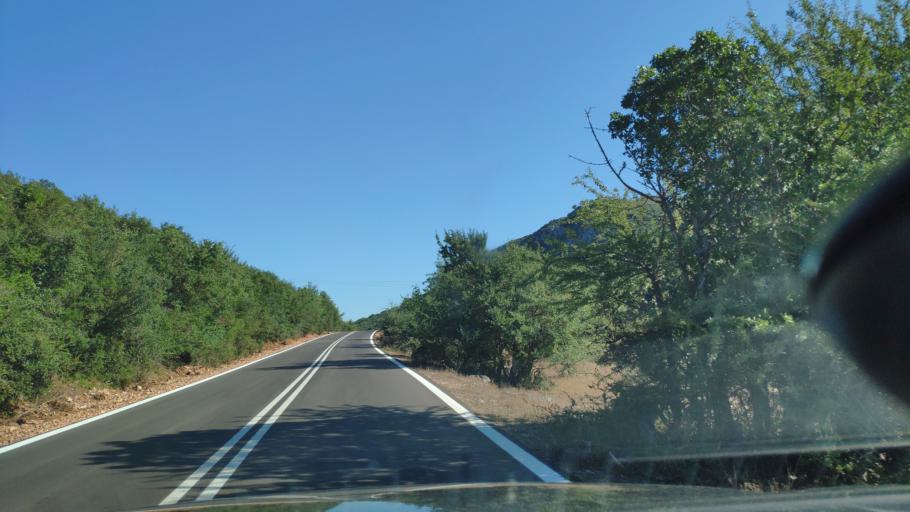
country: GR
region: West Greece
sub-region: Nomos Aitolias kai Akarnanias
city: Fitiai
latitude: 38.6759
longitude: 21.1370
